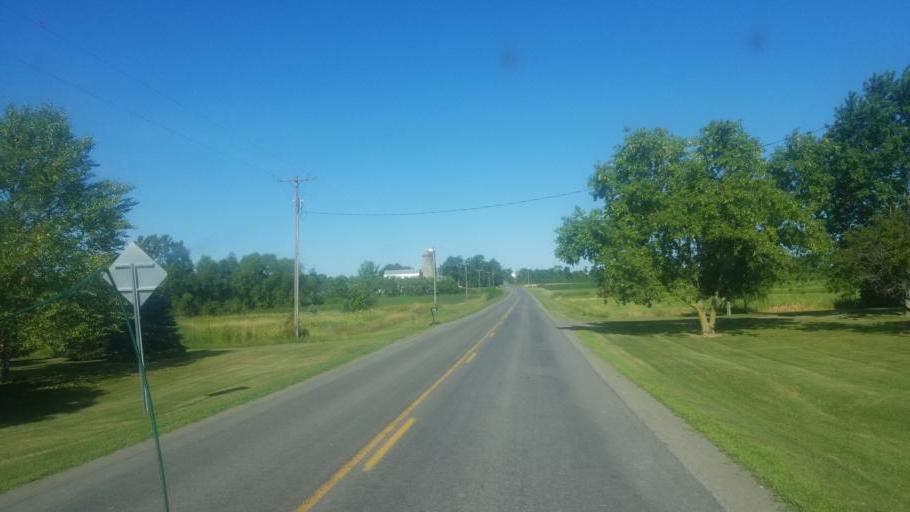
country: US
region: New York
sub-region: Ontario County
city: Canandaigua
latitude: 42.8373
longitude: -77.1697
